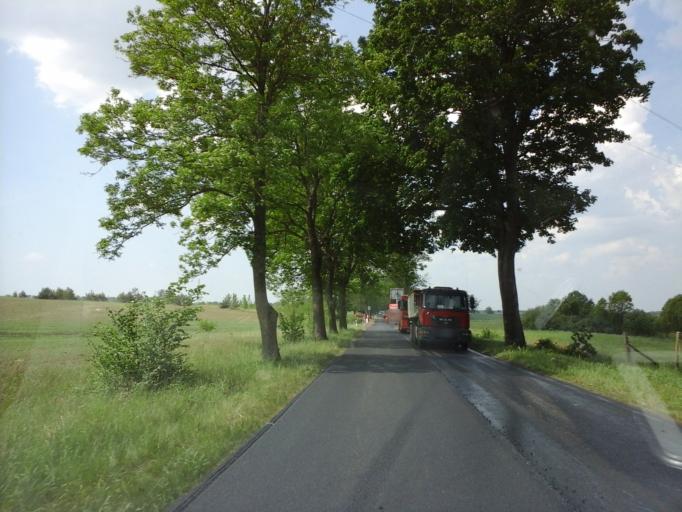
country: PL
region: West Pomeranian Voivodeship
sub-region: Powiat choszczenski
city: Recz
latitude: 53.1897
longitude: 15.6242
